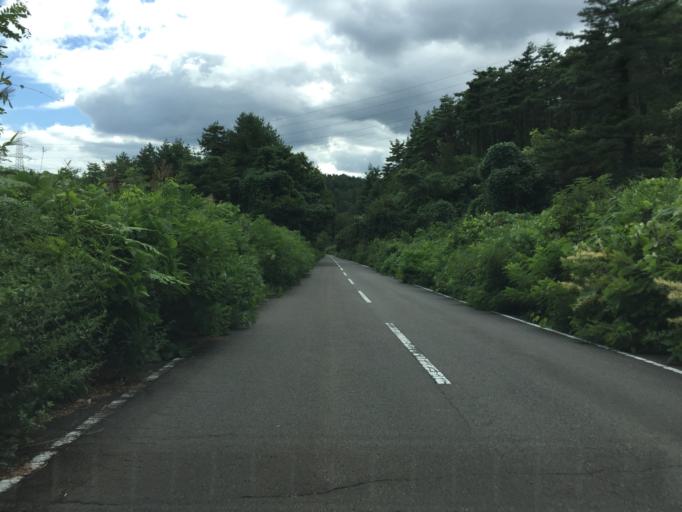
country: JP
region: Fukushima
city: Nihommatsu
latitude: 37.6423
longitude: 140.4128
